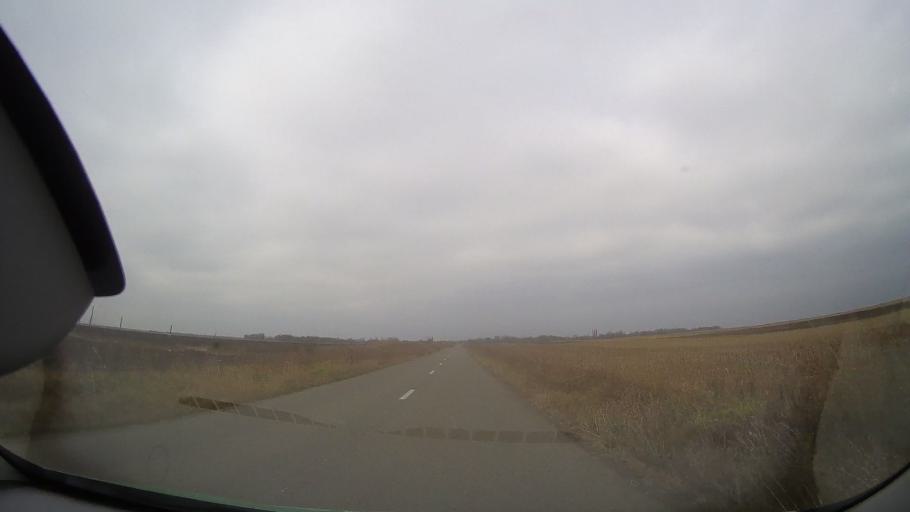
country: RO
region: Buzau
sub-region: Comuna Scutelnici
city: Scutelnici
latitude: 44.8668
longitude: 26.8930
